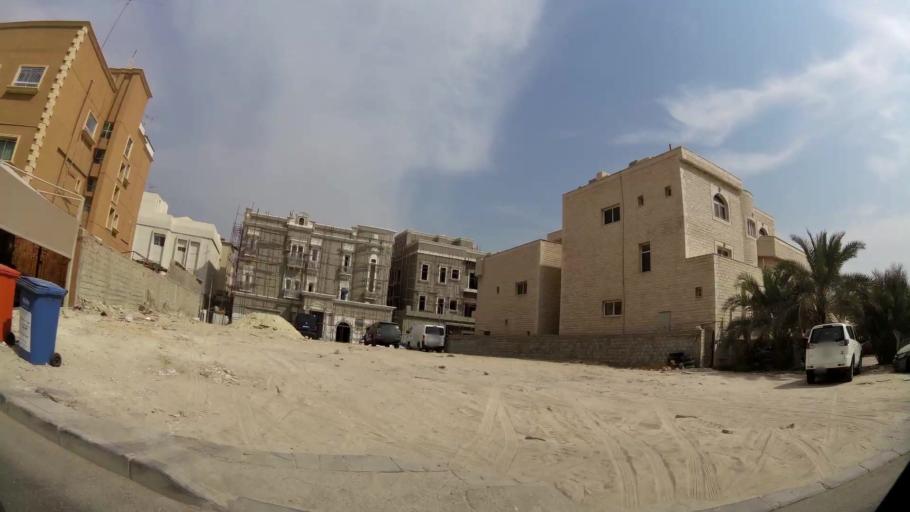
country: KW
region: Al Asimah
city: Ad Dasmah
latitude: 29.3514
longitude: 47.9908
